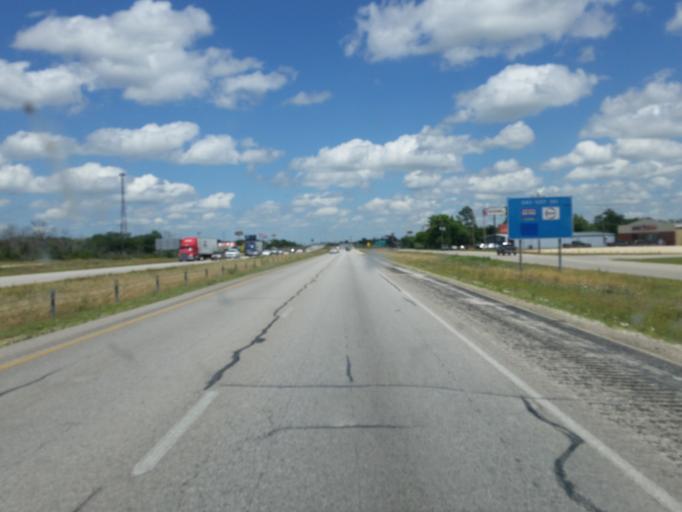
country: US
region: Texas
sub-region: Callahan County
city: Clyde
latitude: 32.4133
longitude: -99.4981
